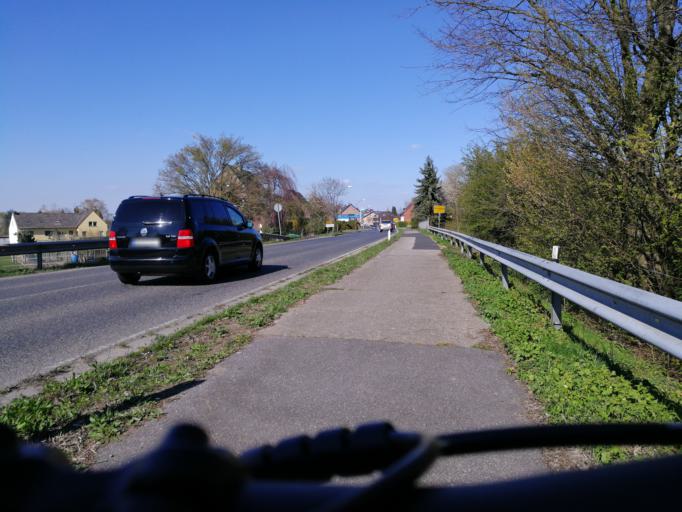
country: DE
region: North Rhine-Westphalia
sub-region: Regierungsbezirk Dusseldorf
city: Neuss
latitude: 51.1727
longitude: 6.7379
